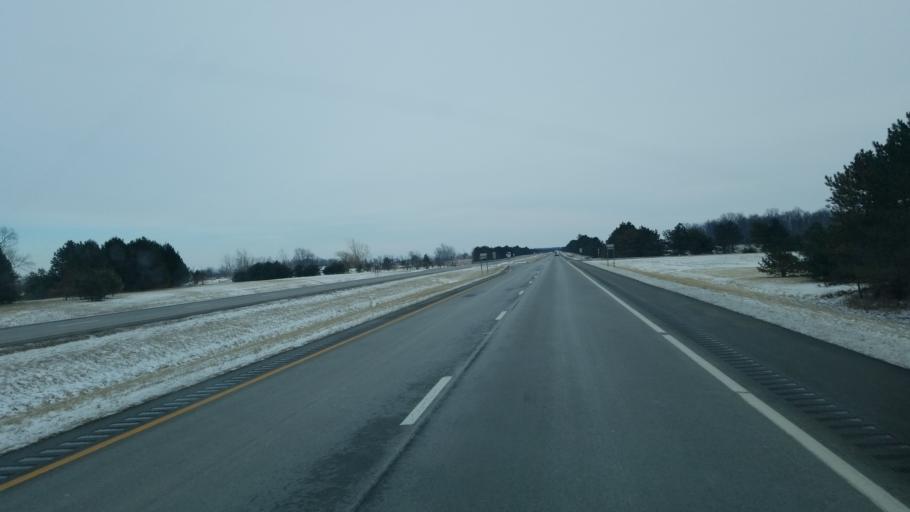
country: US
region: Ohio
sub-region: Wyandot County
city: Carey
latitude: 40.9573
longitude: -83.4489
